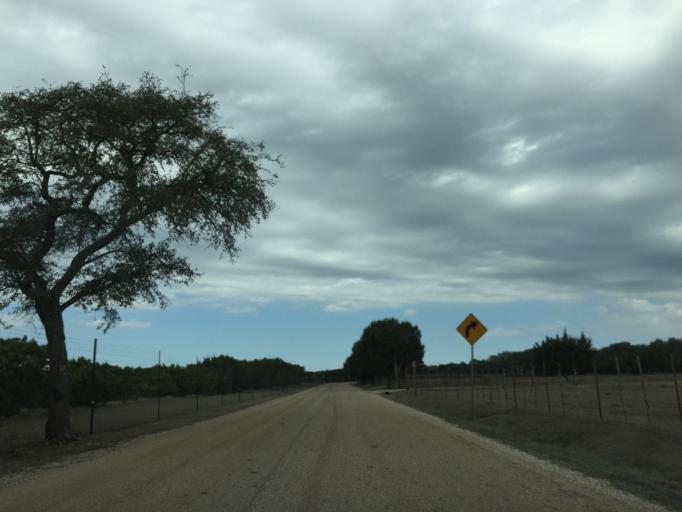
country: US
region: Texas
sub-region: Burnet County
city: Bertram
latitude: 30.6509
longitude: -98.0150
